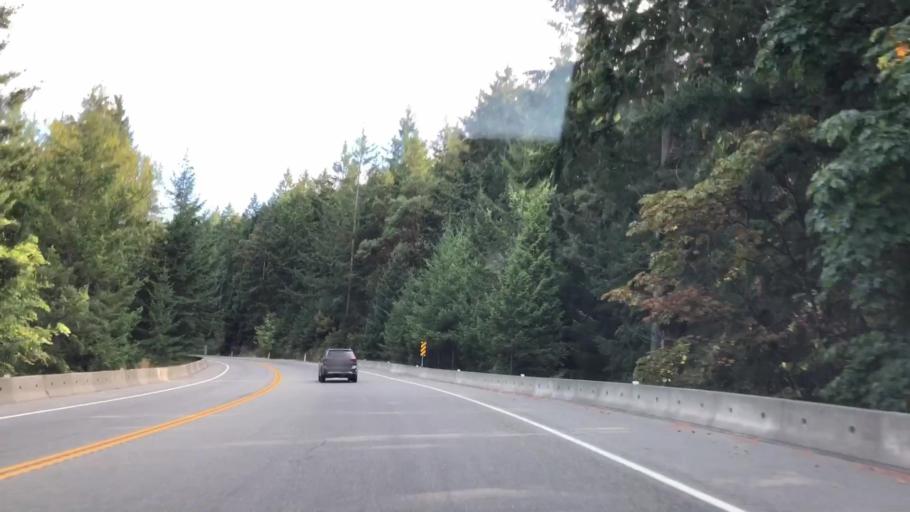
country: CA
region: British Columbia
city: Langford
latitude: 48.5822
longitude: -123.5309
